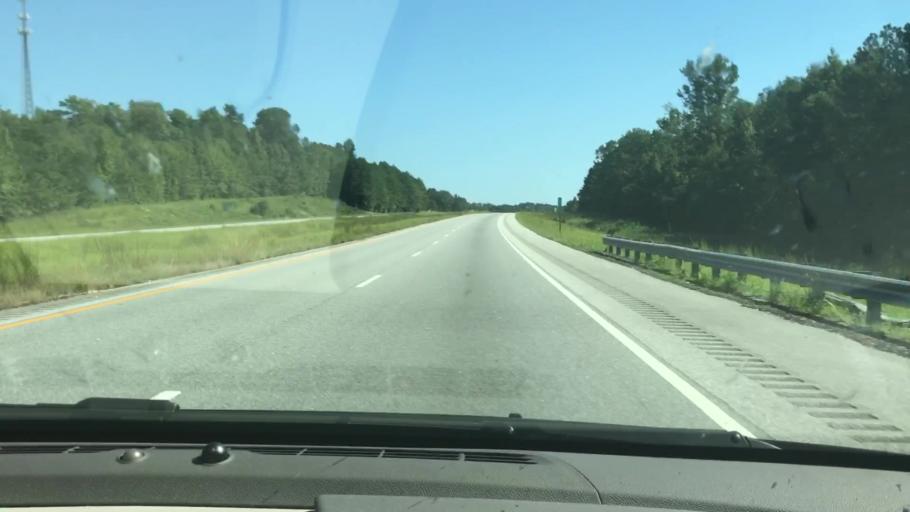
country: US
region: Alabama
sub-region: Russell County
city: Ladonia
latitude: 32.3874
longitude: -85.0782
